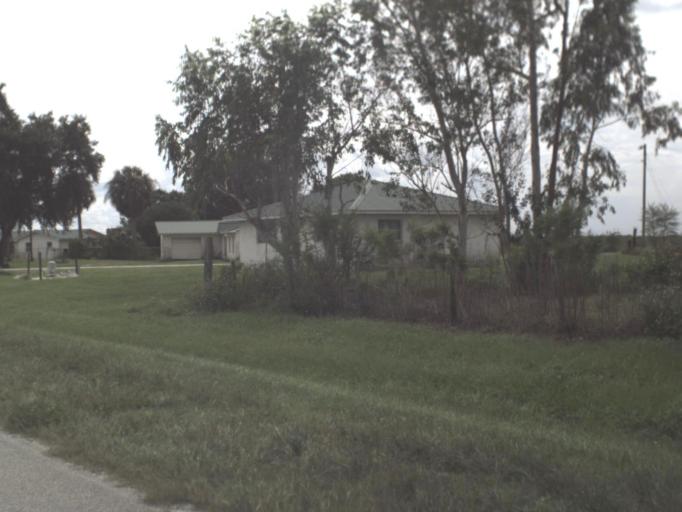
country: US
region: Florida
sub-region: DeSoto County
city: Southeast Arcadia
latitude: 27.1056
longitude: -81.7949
